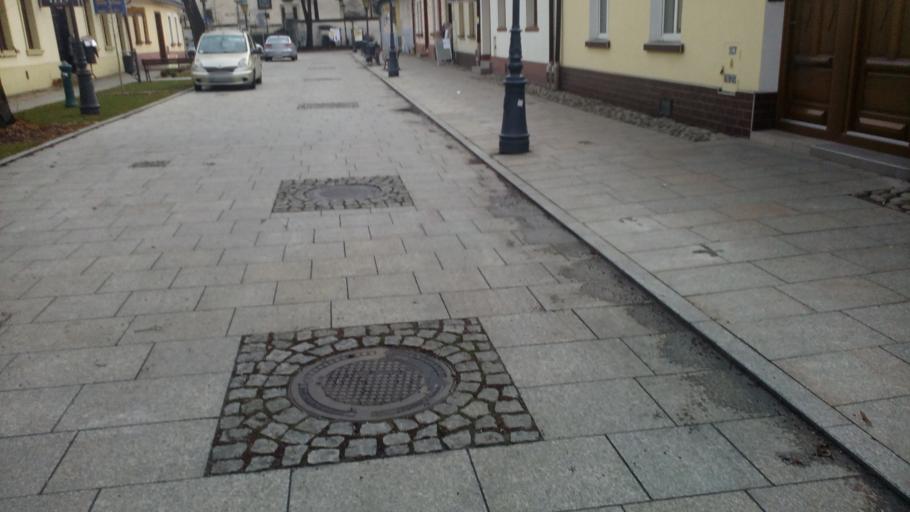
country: PL
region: Lesser Poland Voivodeship
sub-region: Powiat nowosadecki
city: Stary Sacz
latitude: 49.5624
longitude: 20.6353
